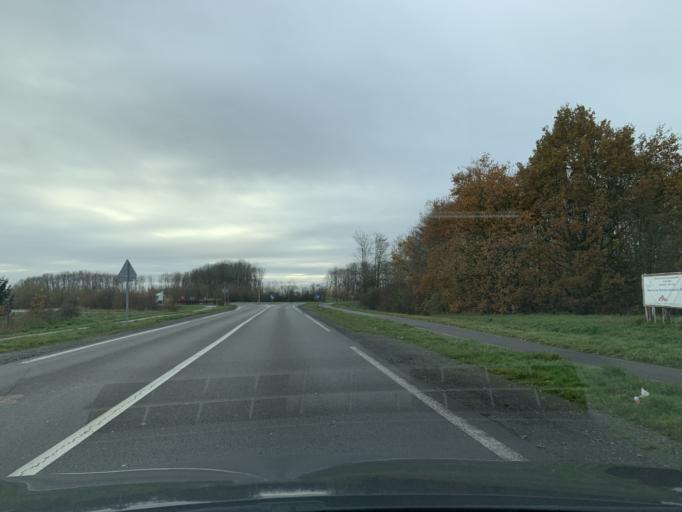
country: FR
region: Nord-Pas-de-Calais
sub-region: Departement du Nord
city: Goeulzin
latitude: 50.3274
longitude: 3.1095
